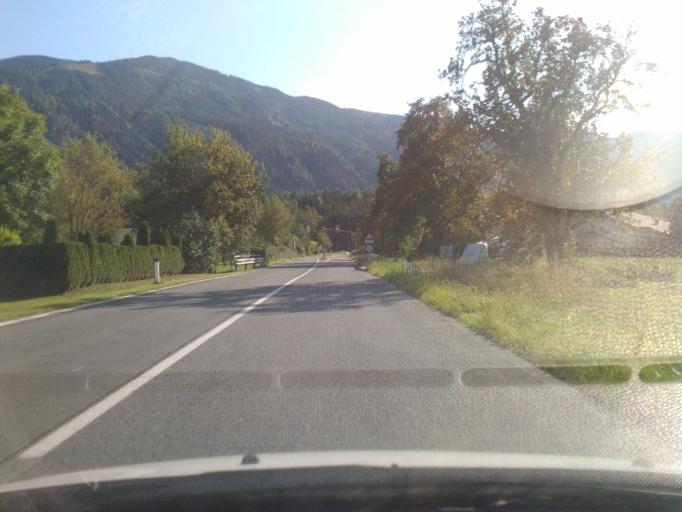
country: AT
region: Carinthia
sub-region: Politischer Bezirk Villach Land
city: Arnoldstein
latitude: 46.5497
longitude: 13.7870
